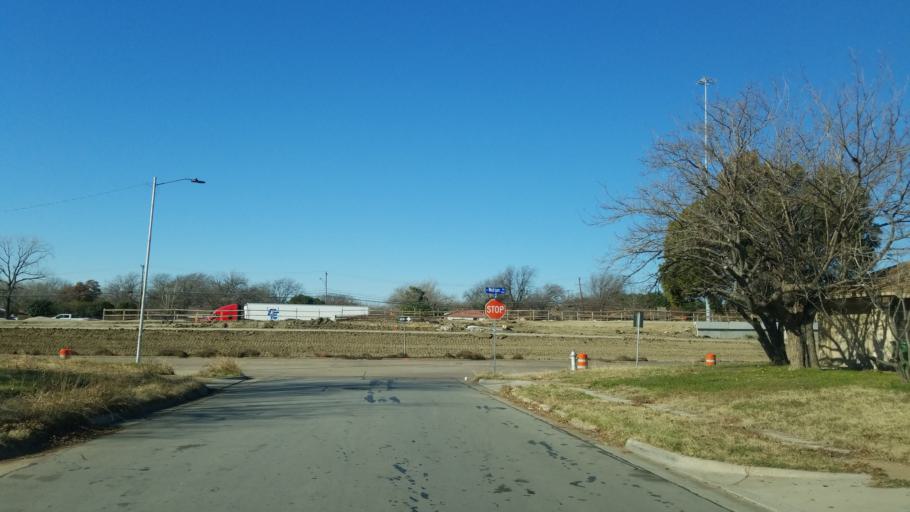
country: US
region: Texas
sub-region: Tarrant County
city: Arlington
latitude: 32.7314
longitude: -97.0615
